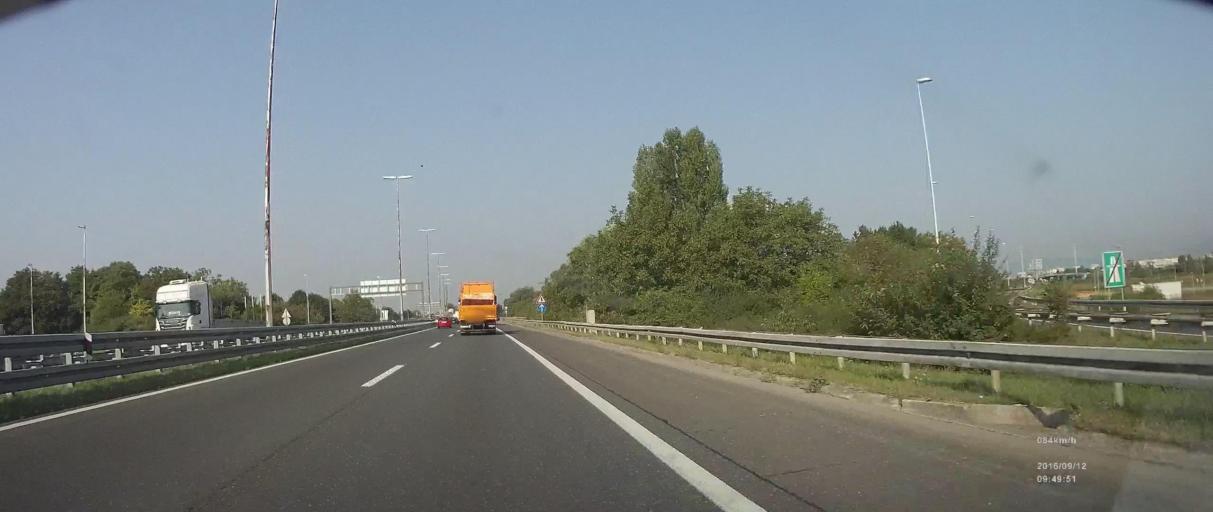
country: HR
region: Grad Zagreb
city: Odra
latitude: 45.7529
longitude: 15.9951
